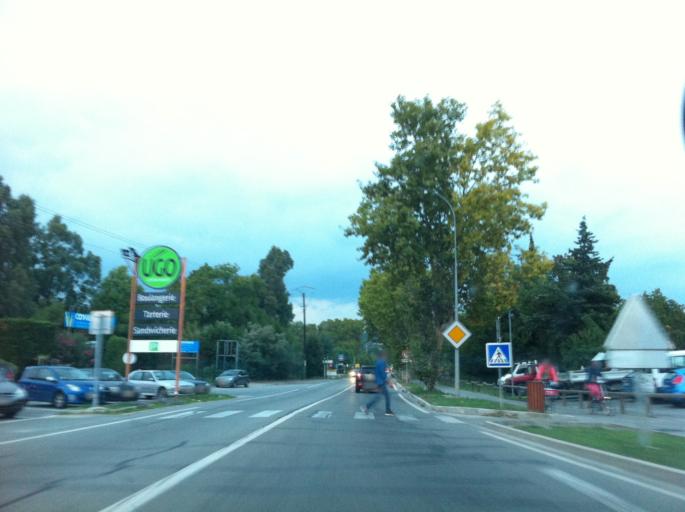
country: FR
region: Provence-Alpes-Cote d'Azur
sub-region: Departement du Var
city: Gassin
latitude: 43.2748
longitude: 6.5747
